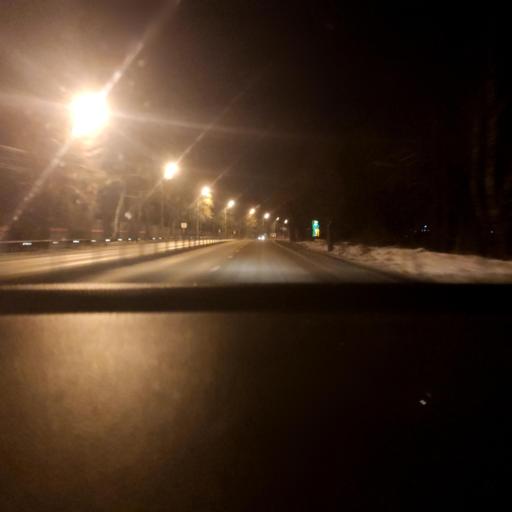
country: RU
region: Moskovskaya
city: Zhavoronki
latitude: 55.6578
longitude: 37.1160
